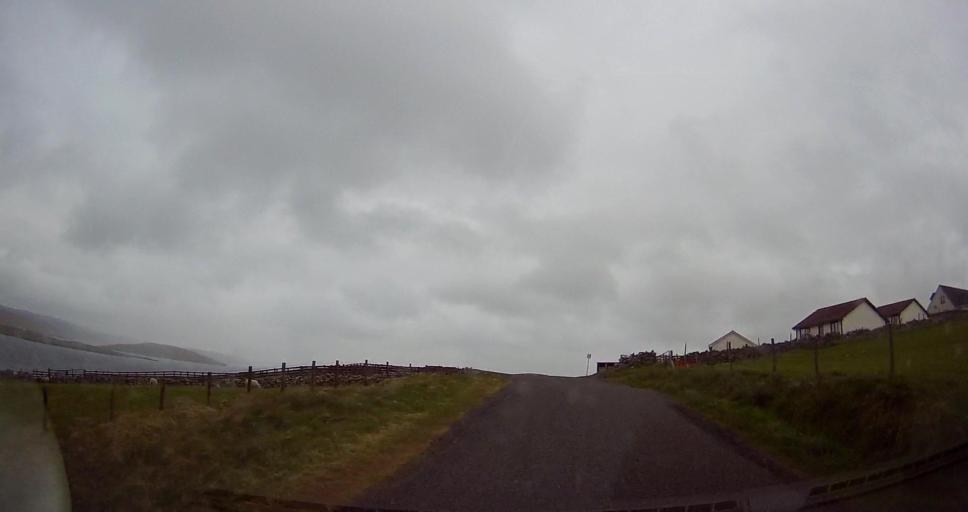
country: GB
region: Scotland
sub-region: Shetland Islands
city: Lerwick
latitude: 60.3879
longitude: -1.3719
